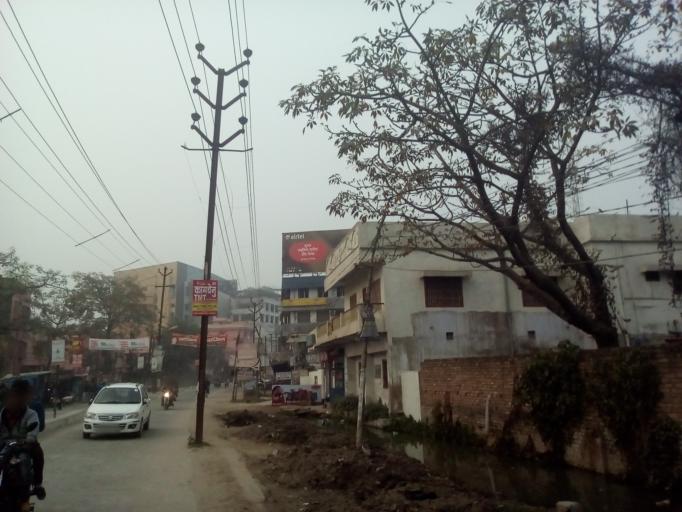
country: IN
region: Bihar
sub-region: Muzaffarpur
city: Muzaffarpur
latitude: 26.1085
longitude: 85.3966
